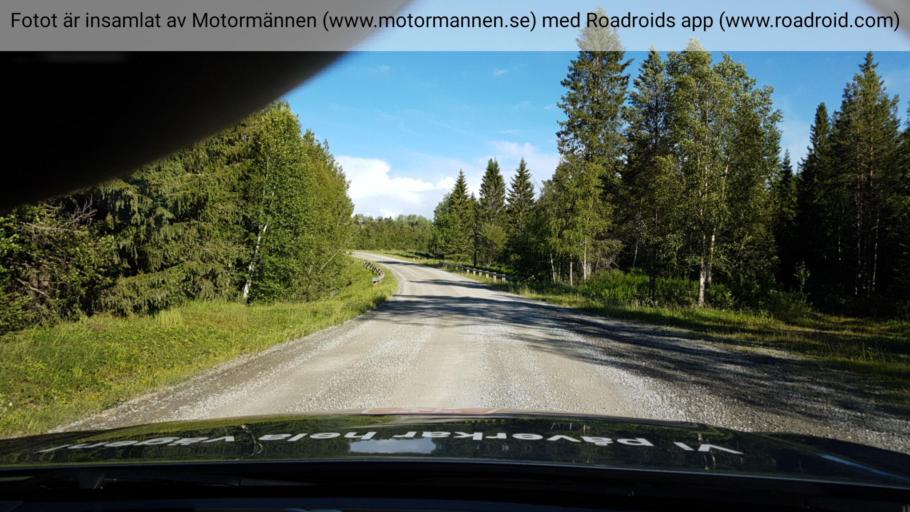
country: SE
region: Jaemtland
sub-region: Bergs Kommun
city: Hoverberg
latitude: 63.0302
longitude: 14.3572
